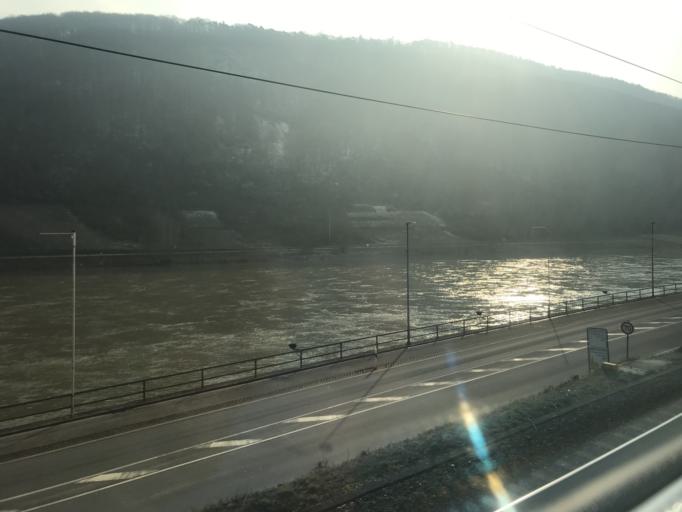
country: DE
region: Rheinland-Pfalz
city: Winningen
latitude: 50.3157
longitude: 7.5216
